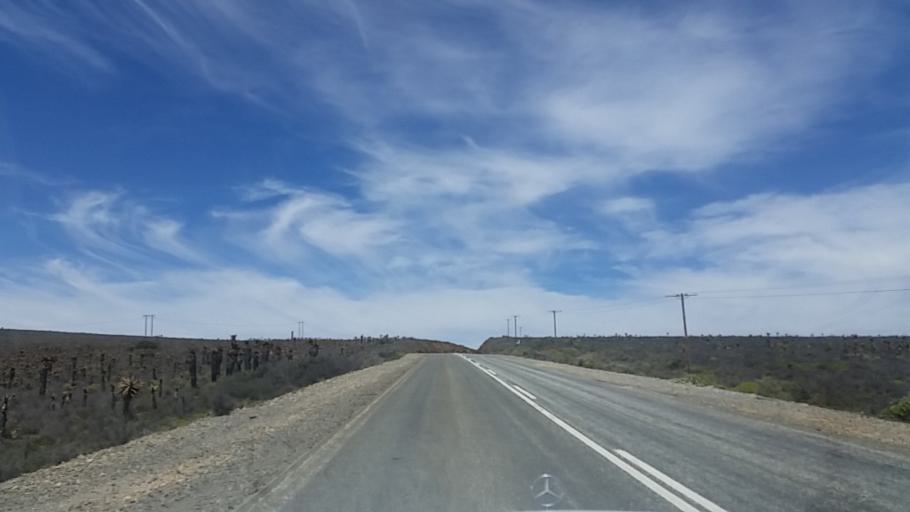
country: ZA
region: Eastern Cape
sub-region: Cacadu District Municipality
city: Willowmore
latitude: -33.5792
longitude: 23.1671
